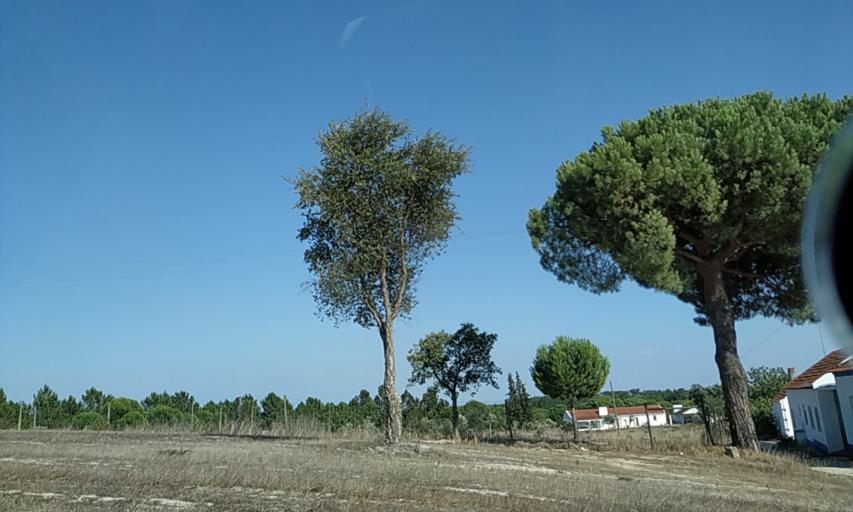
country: PT
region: Santarem
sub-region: Coruche
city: Coruche
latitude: 38.8206
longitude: -8.5685
